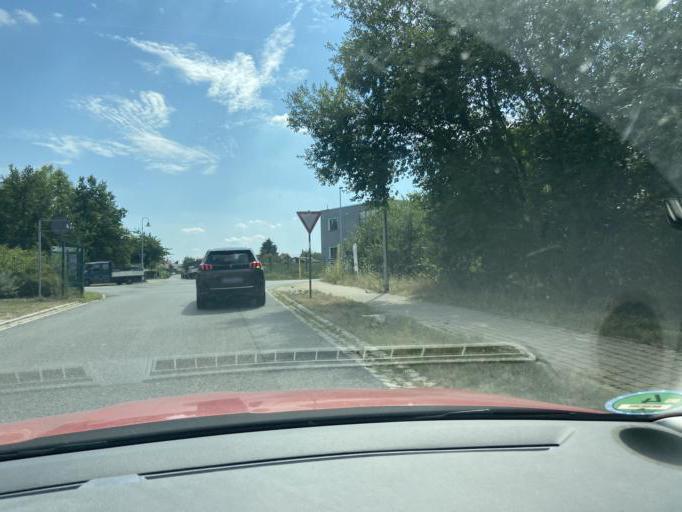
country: DE
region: Saxony
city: Tharandt
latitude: 51.0368
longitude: 13.5865
